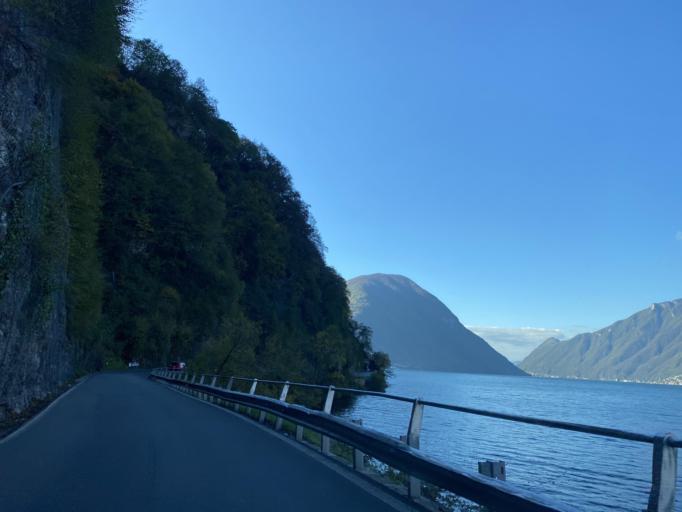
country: IT
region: Lombardy
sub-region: Provincia di Como
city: Porlezza
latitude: 46.0194
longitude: 9.1151
